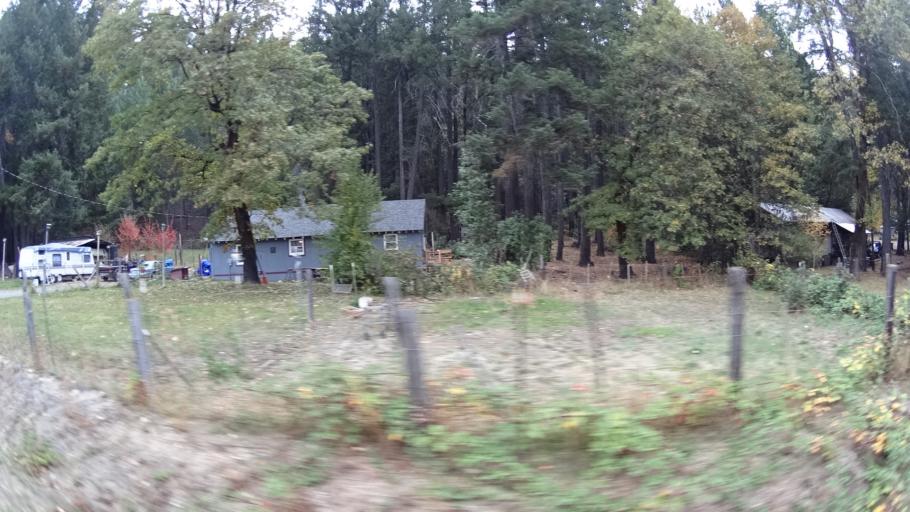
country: US
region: California
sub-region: Siskiyou County
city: Happy Camp
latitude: 41.8696
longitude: -123.4051
